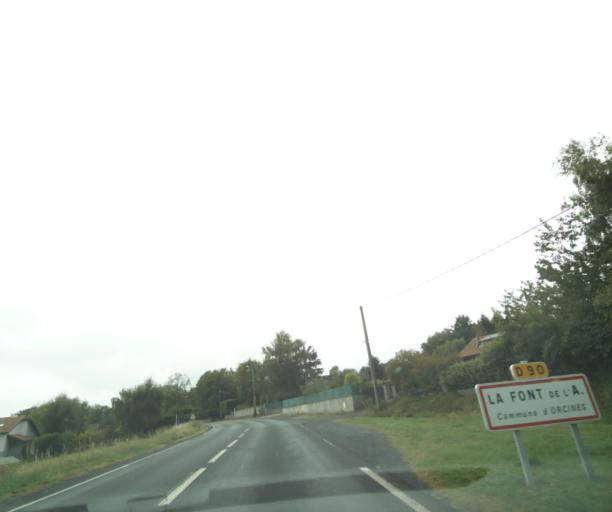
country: FR
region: Auvergne
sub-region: Departement du Puy-de-Dome
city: Orcines
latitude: 45.7725
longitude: 3.0095
